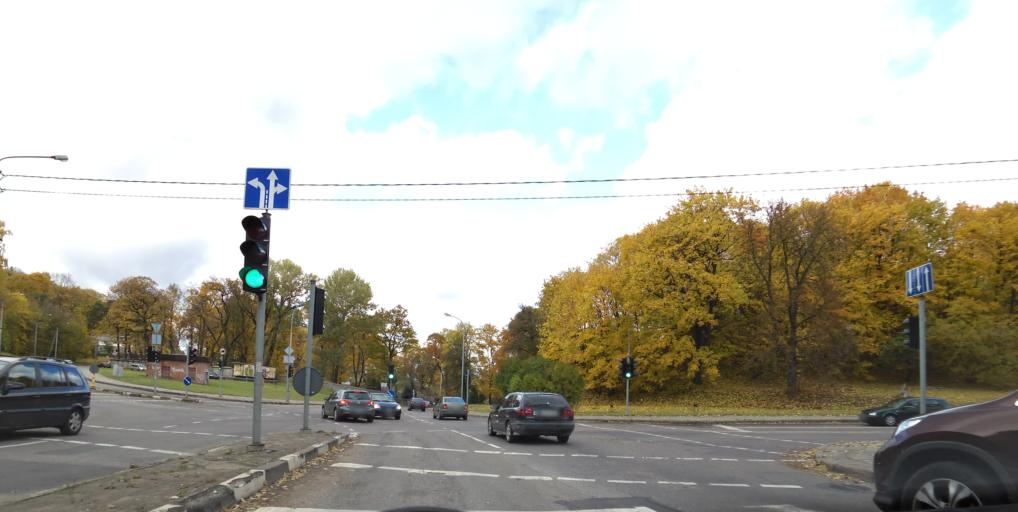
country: LT
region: Vilnius County
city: Rasos
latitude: 54.6663
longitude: 25.3055
